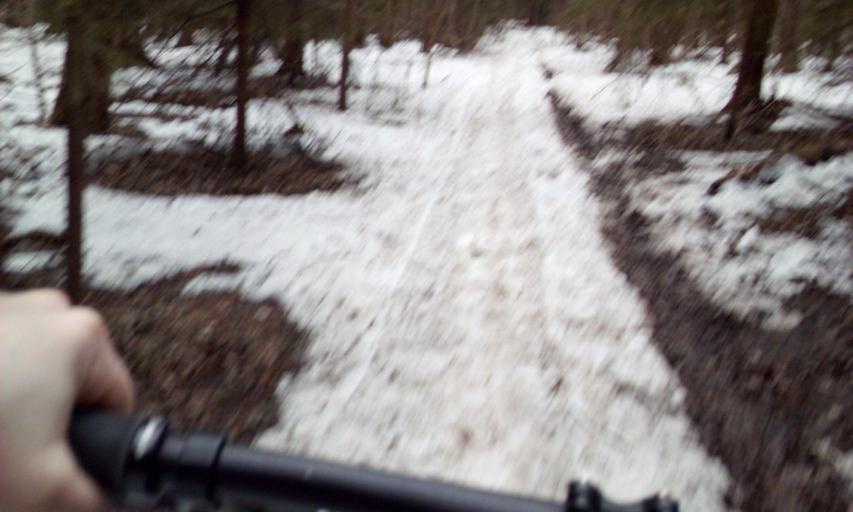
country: RU
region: Moskovskaya
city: Annino
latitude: 55.5520
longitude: 37.2695
